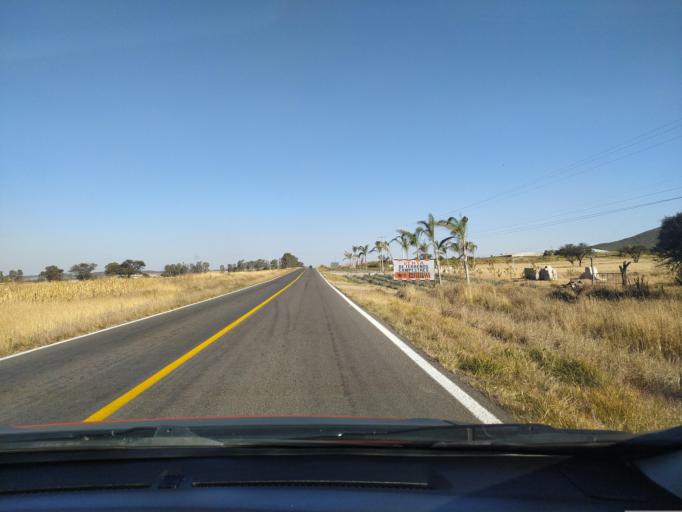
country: MX
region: Jalisco
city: San Miguel el Alto
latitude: 21.0167
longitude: -102.4707
